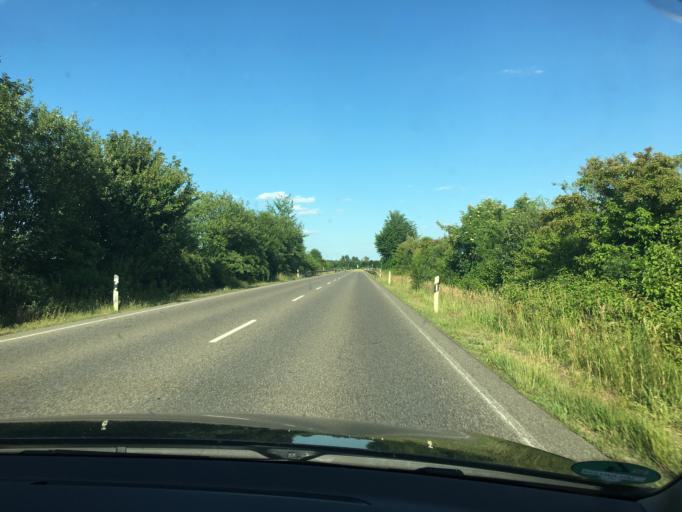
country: DE
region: North Rhine-Westphalia
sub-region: Regierungsbezirk Koln
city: Kerpen
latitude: 50.8532
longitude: 6.6967
